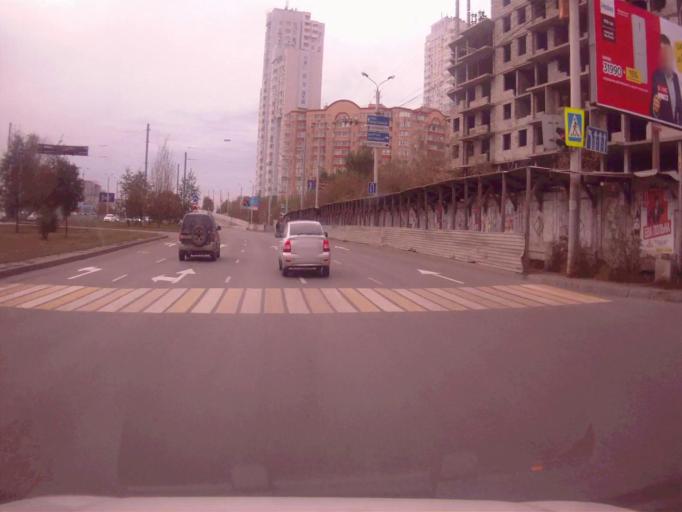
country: RU
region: Chelyabinsk
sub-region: Gorod Chelyabinsk
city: Chelyabinsk
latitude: 55.1743
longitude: 61.3946
